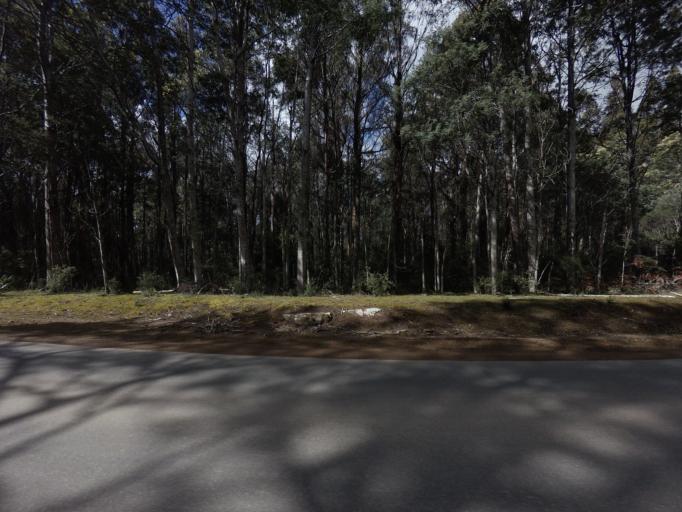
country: AU
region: Tasmania
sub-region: Huon Valley
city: Geeveston
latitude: -43.3459
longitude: 146.9616
